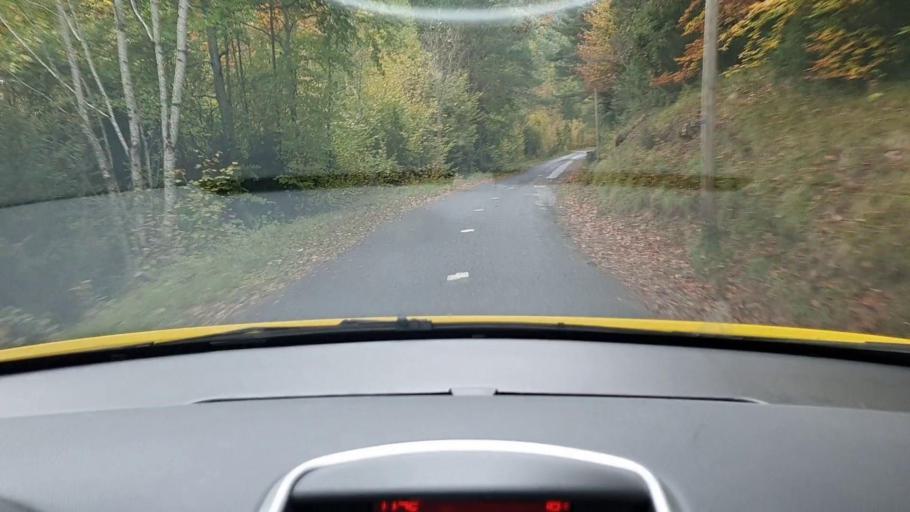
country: FR
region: Languedoc-Roussillon
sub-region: Departement de la Lozere
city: Meyrueis
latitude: 44.1207
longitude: 3.4342
